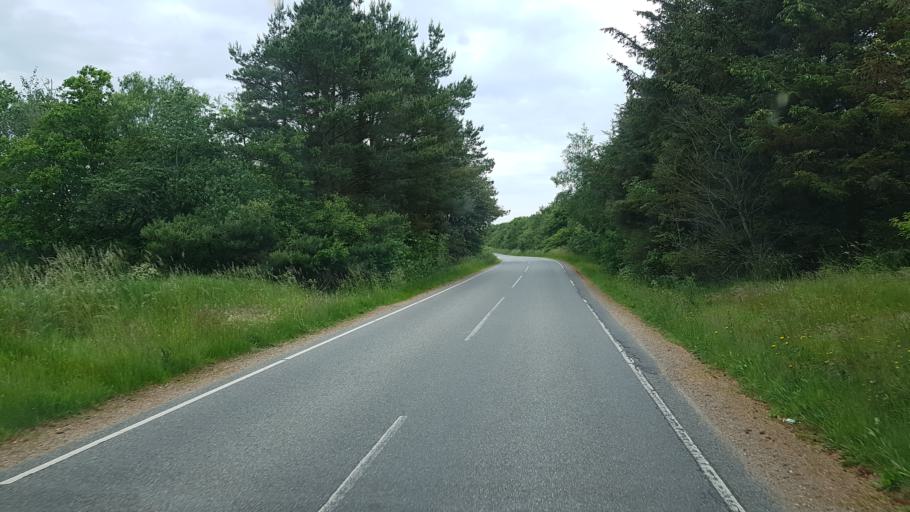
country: DK
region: South Denmark
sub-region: Varde Kommune
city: Oksbol
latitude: 55.6654
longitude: 8.3068
